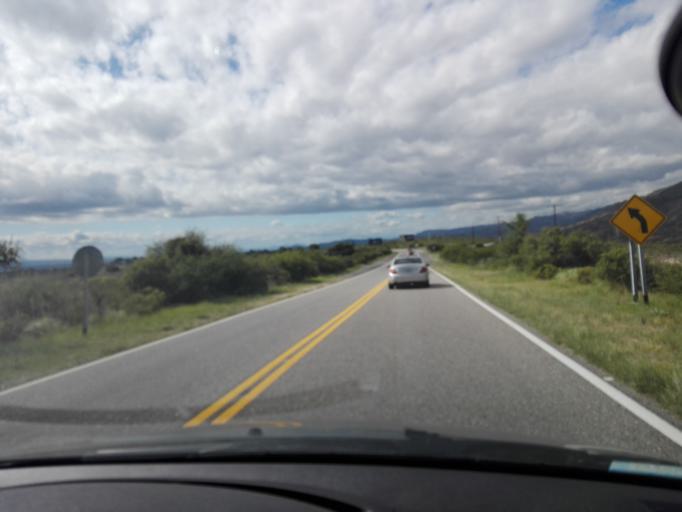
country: AR
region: Cordoba
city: Mina Clavero
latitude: -31.7465
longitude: -64.9333
